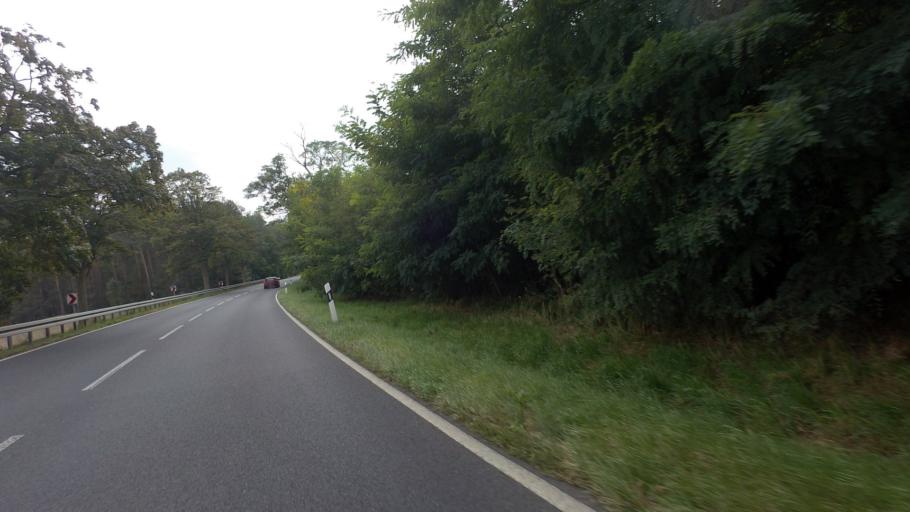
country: DE
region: Brandenburg
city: Sonnewalde
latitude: 51.7436
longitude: 13.6814
